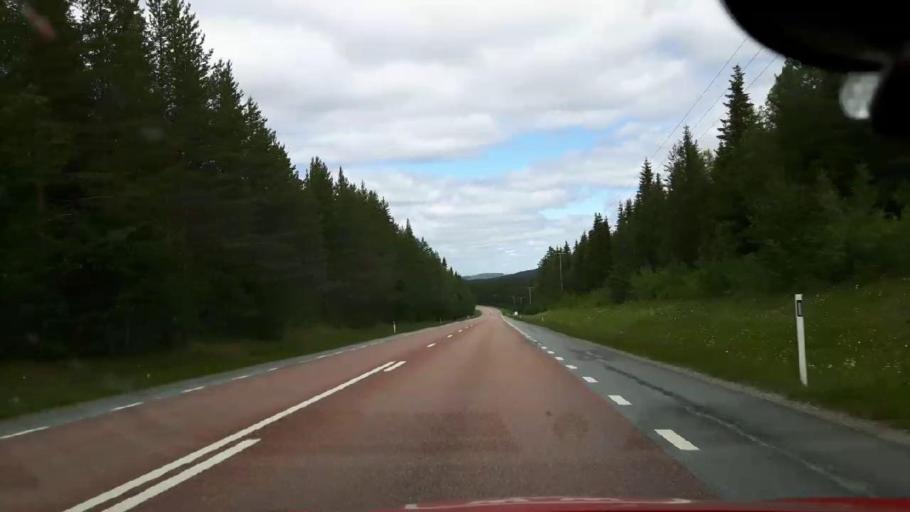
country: SE
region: Jaemtland
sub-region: Braecke Kommun
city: Braecke
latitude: 62.8083
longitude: 15.3668
